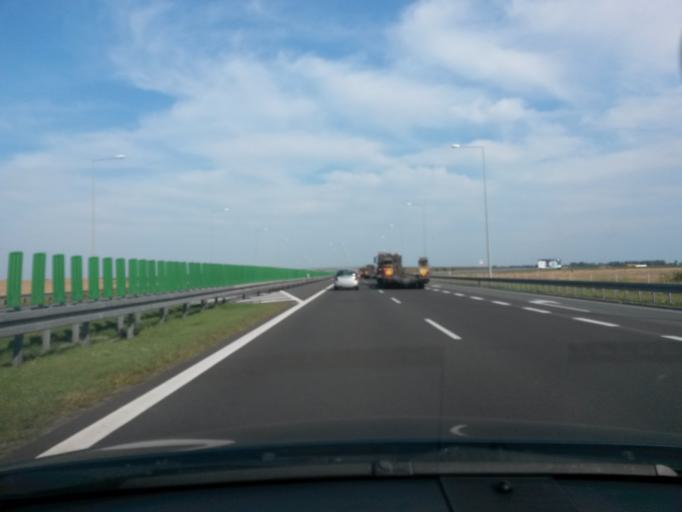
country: PL
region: Greater Poland Voivodeship
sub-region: Powiat slupecki
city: Strzalkowo
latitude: 52.2557
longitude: 17.8115
